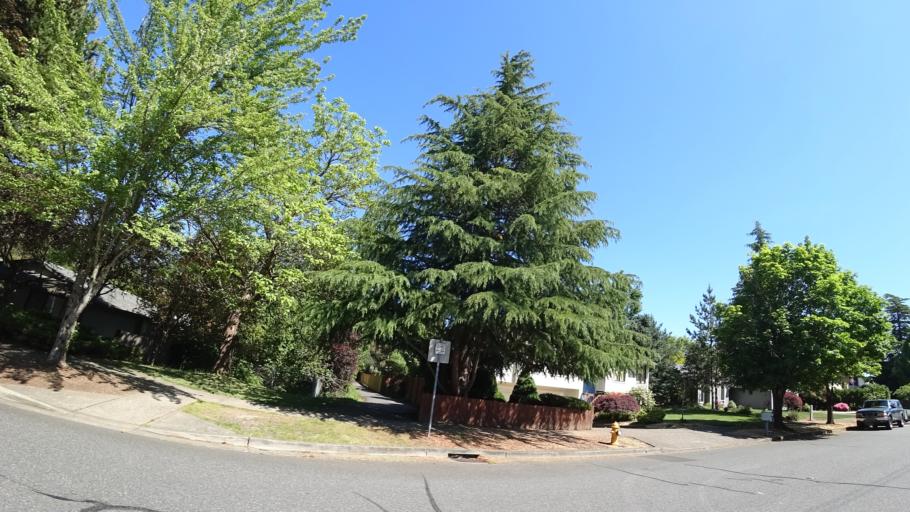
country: US
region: Oregon
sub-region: Washington County
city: Beaverton
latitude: 45.4460
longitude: -122.8107
